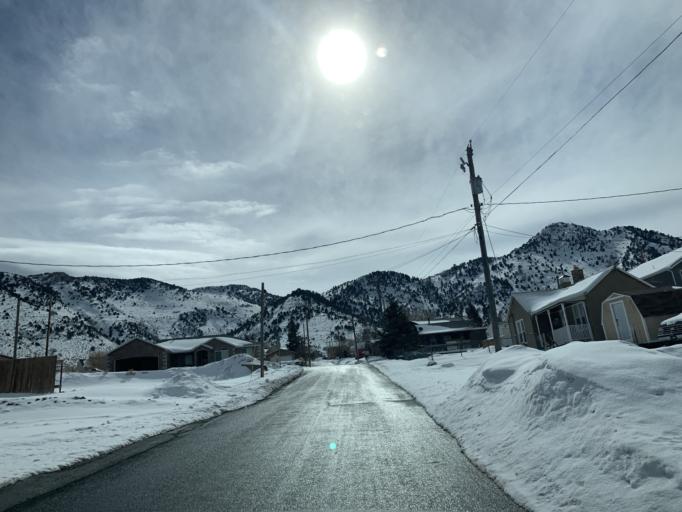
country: US
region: Utah
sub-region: Utah County
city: Genola
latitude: 39.9536
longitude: -112.1178
